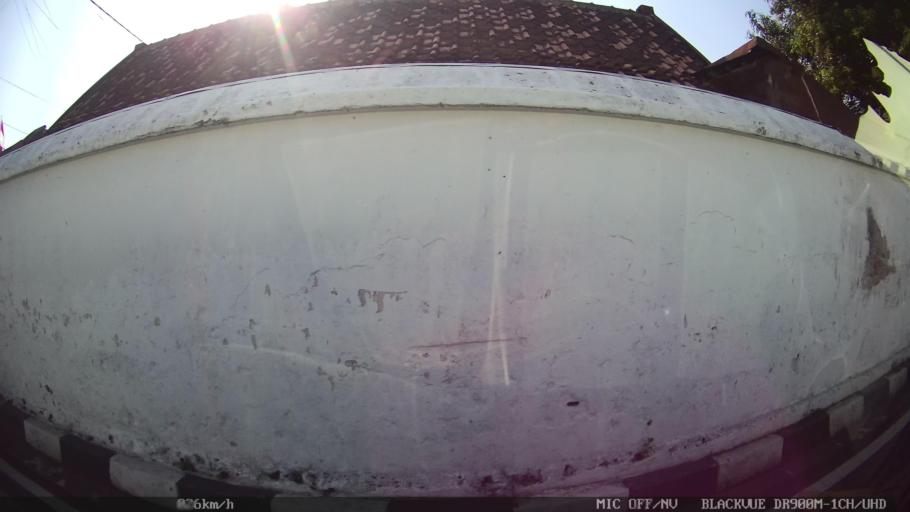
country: ID
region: Daerah Istimewa Yogyakarta
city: Yogyakarta
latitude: -7.8093
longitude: 110.3609
